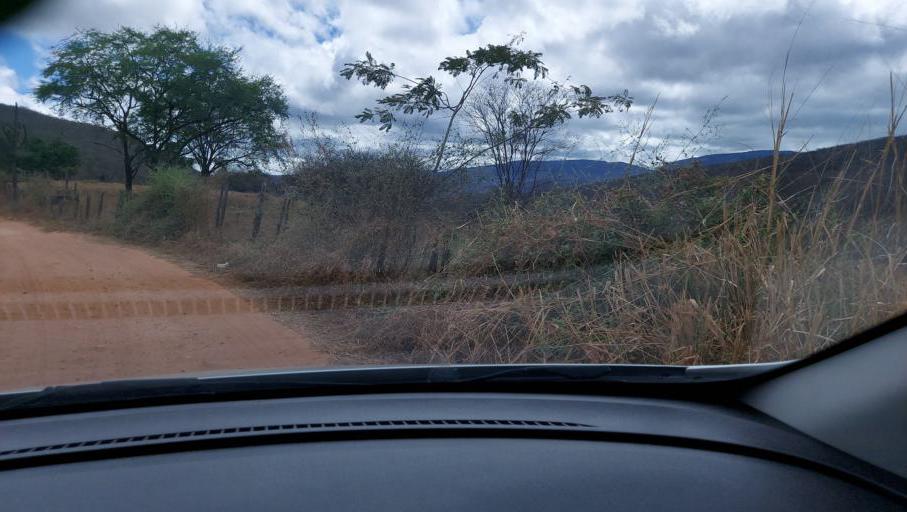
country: BR
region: Bahia
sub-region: Oliveira Dos Brejinhos
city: Beira Rio
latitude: -12.0761
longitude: -42.5414
